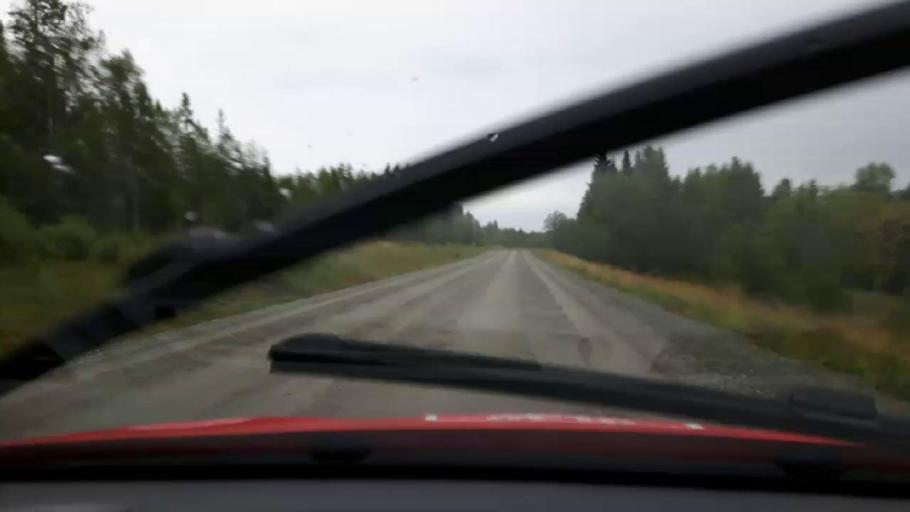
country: SE
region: Jaemtland
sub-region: Are Kommun
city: Are
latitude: 63.4580
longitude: 12.6397
